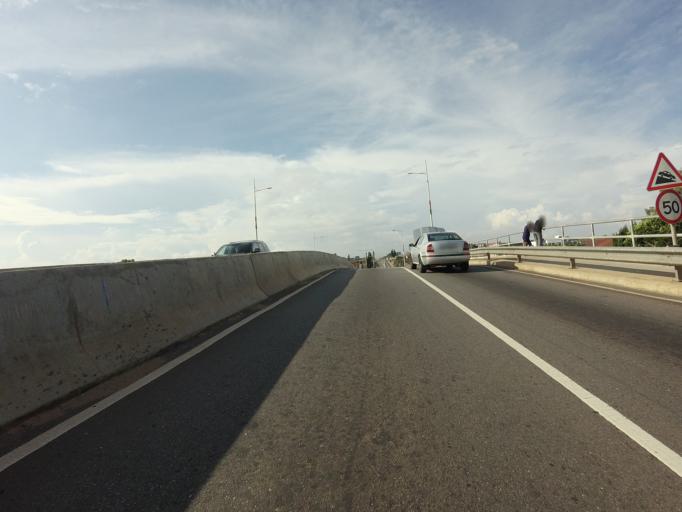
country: GH
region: Greater Accra
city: Medina Estates
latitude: 5.6195
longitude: -0.1527
